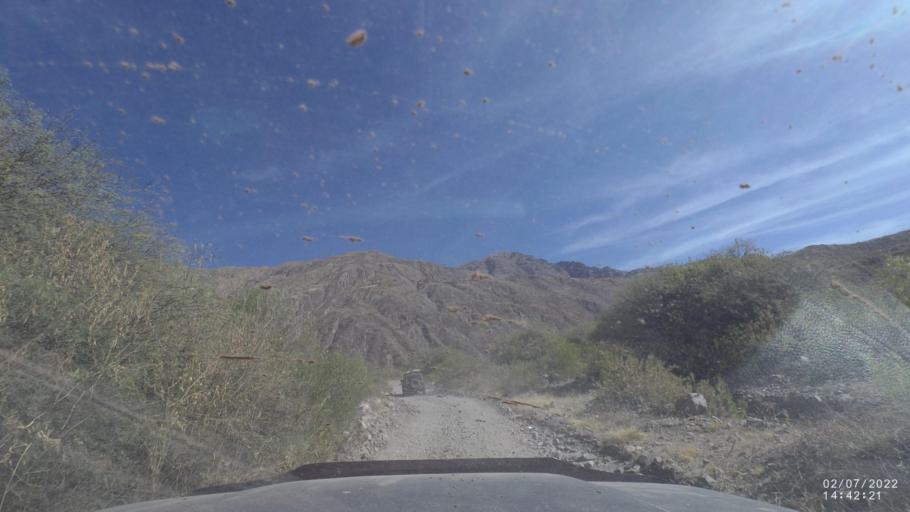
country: BO
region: Cochabamba
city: Irpa Irpa
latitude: -17.8513
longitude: -66.4203
